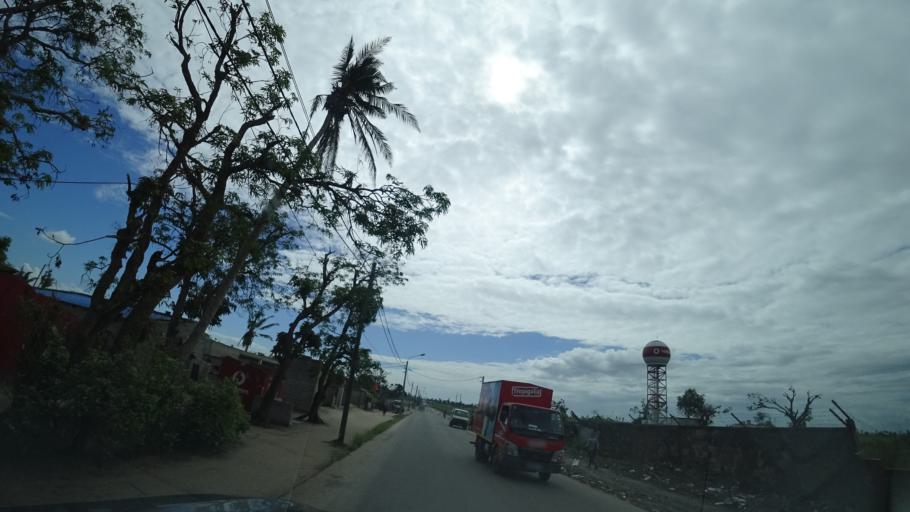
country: MZ
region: Sofala
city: Beira
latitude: -19.7959
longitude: 34.8926
